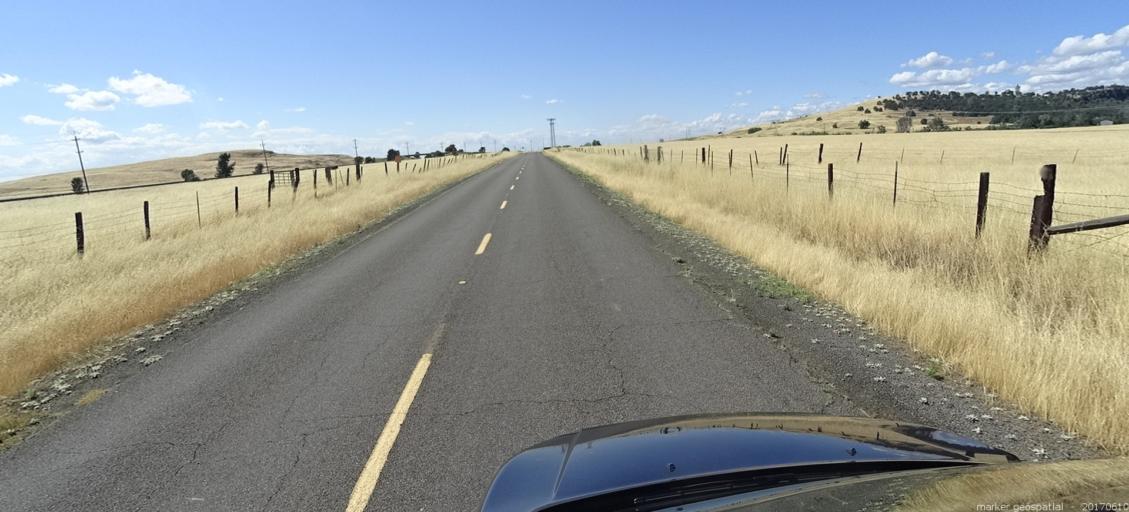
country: US
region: California
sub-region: Butte County
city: Thermalito
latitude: 39.5630
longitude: -121.6037
